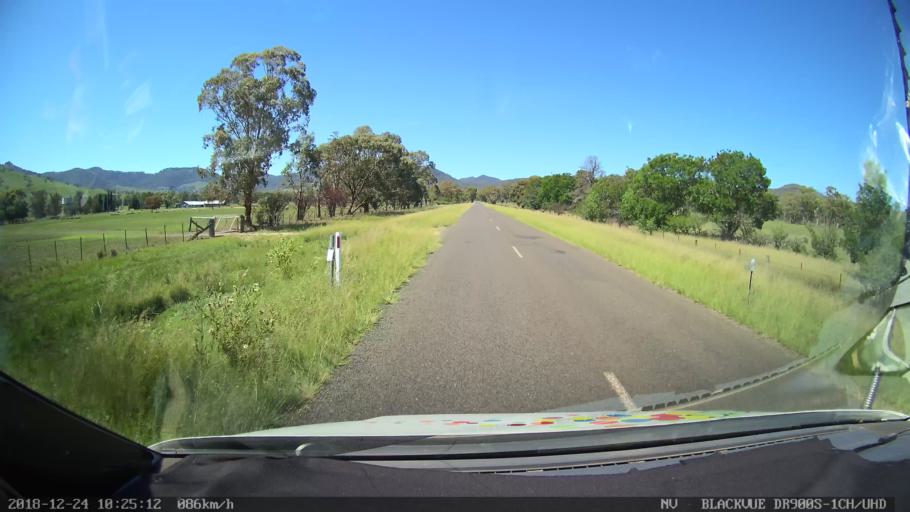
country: AU
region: New South Wales
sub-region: Liverpool Plains
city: Quirindi
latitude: -31.7960
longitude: 150.5295
